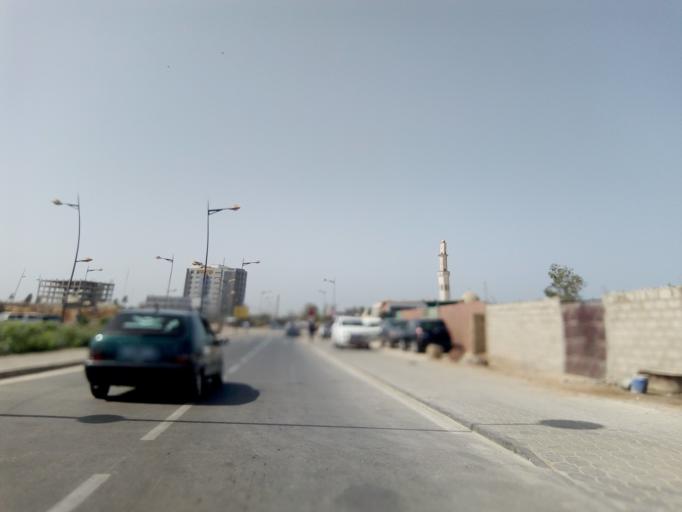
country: SN
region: Dakar
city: Dakar
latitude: 14.7025
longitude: -17.4512
